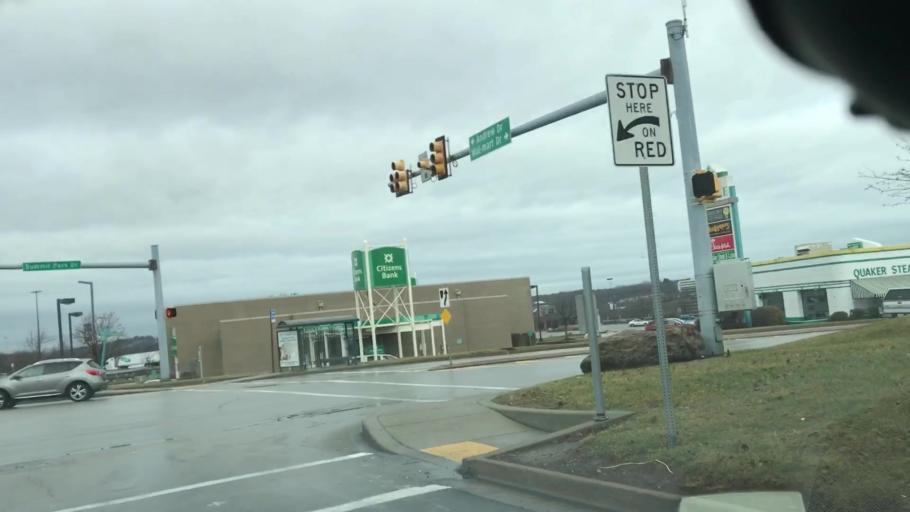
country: US
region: Pennsylvania
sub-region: Allegheny County
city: Oakdale
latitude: 40.4497
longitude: -80.1758
